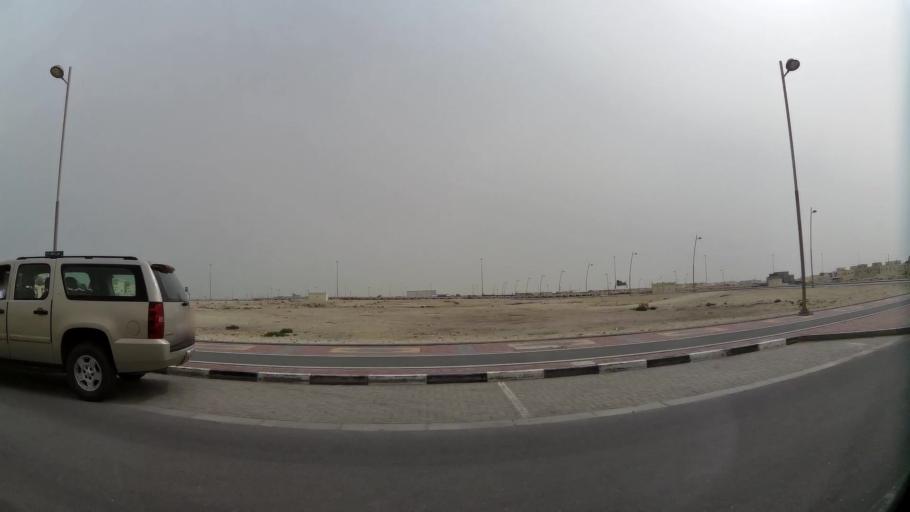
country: QA
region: Baladiyat ad Dawhah
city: Doha
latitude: 25.2280
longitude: 51.5489
